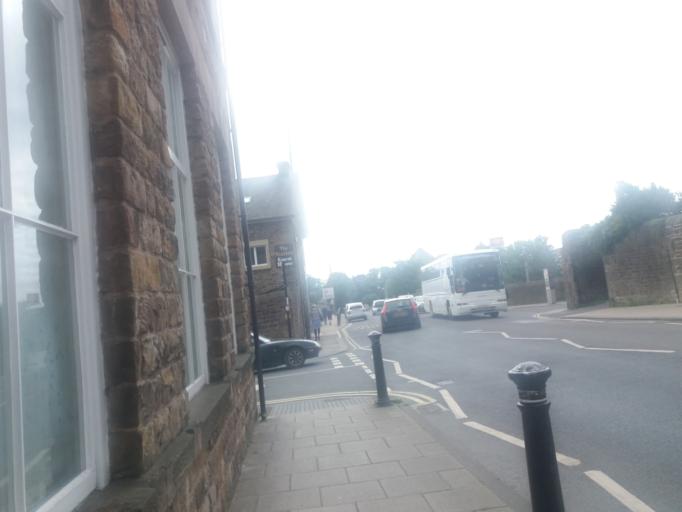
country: GB
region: England
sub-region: Lancashire
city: Lancaster
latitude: 54.0481
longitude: -2.8062
